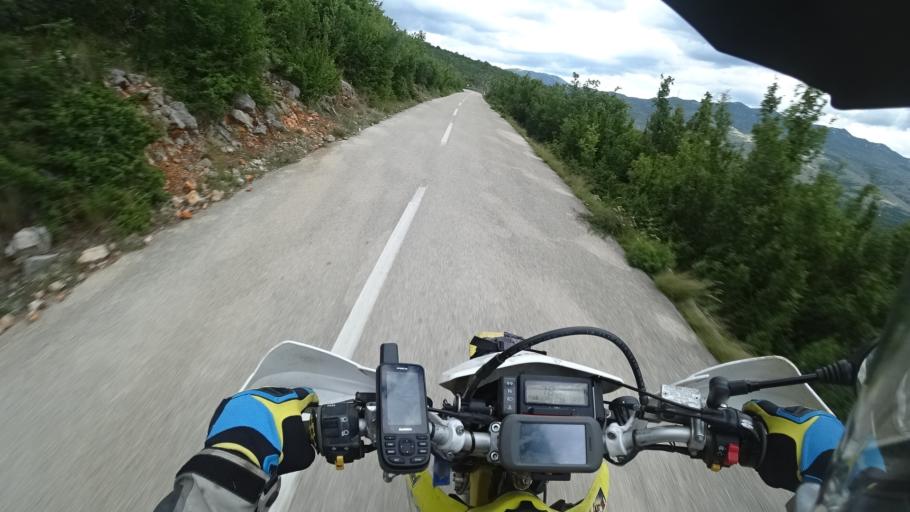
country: HR
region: Zadarska
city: Gracac
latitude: 44.1948
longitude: 15.8777
